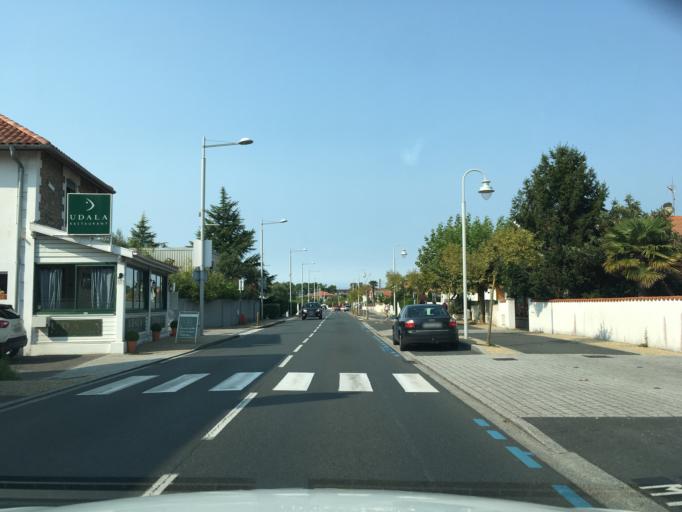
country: FR
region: Aquitaine
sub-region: Departement des Pyrenees-Atlantiques
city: Boucau
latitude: 43.5173
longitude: -1.5017
